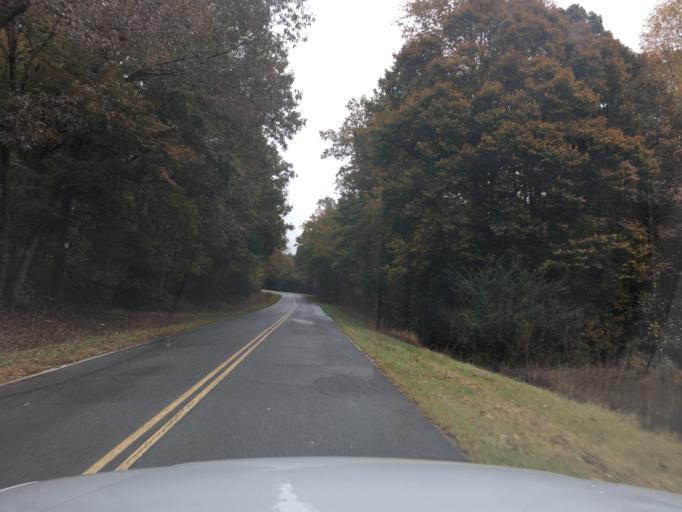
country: US
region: South Carolina
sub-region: Pickens County
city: Central
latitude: 34.7554
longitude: -82.7679
